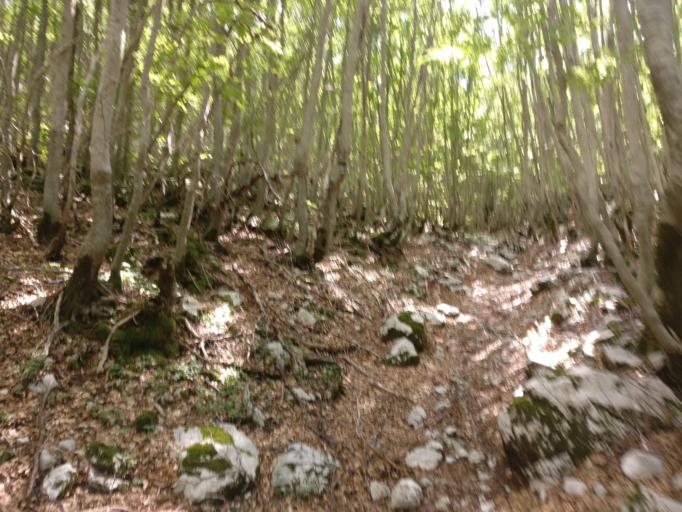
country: ME
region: Kotor
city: Kotor
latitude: 42.4099
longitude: 18.8397
